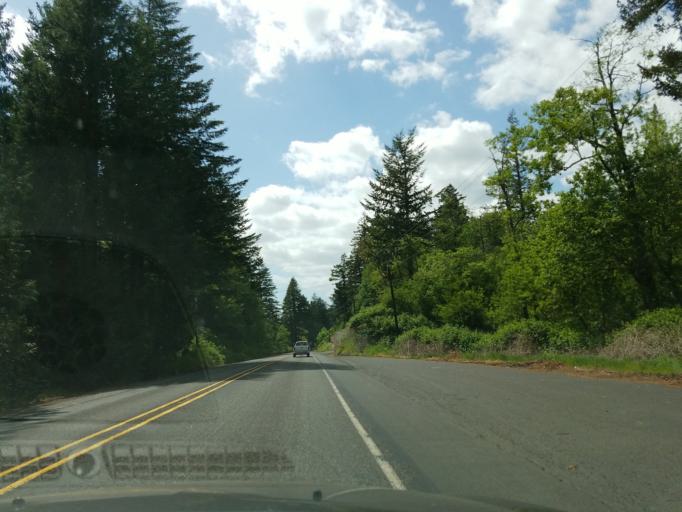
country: US
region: Oregon
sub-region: Hood River County
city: Cascade Locks
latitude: 45.6076
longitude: -122.0758
